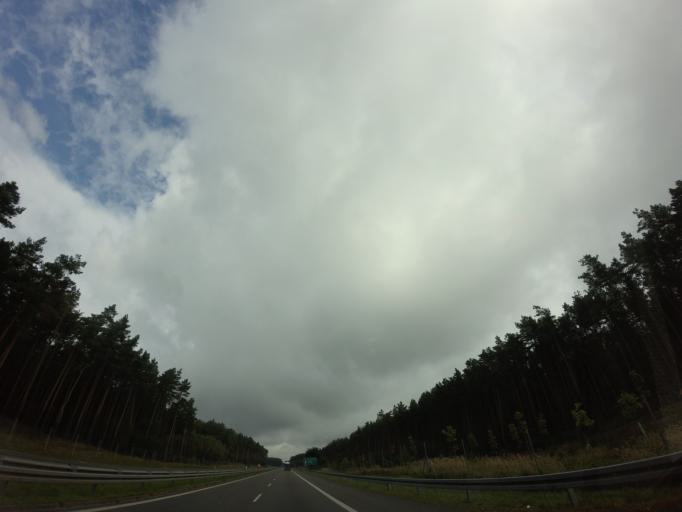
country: PL
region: West Pomeranian Voivodeship
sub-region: Powiat goleniowski
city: Goleniow
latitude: 53.5991
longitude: 14.8246
